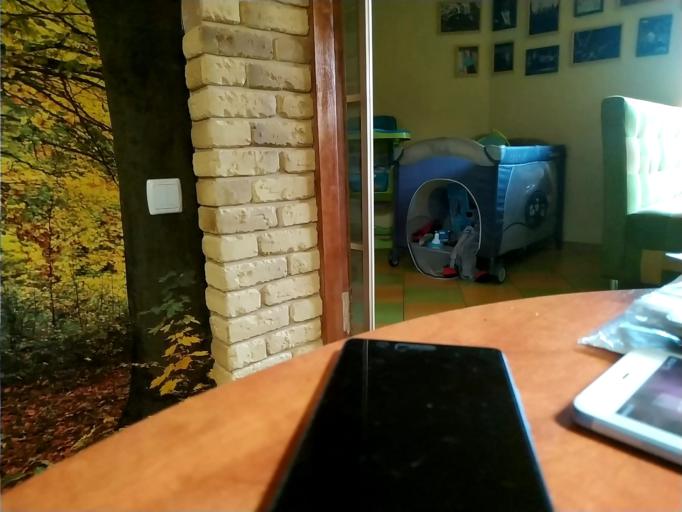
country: RU
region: Kaluga
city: Seredeyskiy
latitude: 53.7879
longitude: 35.3980
